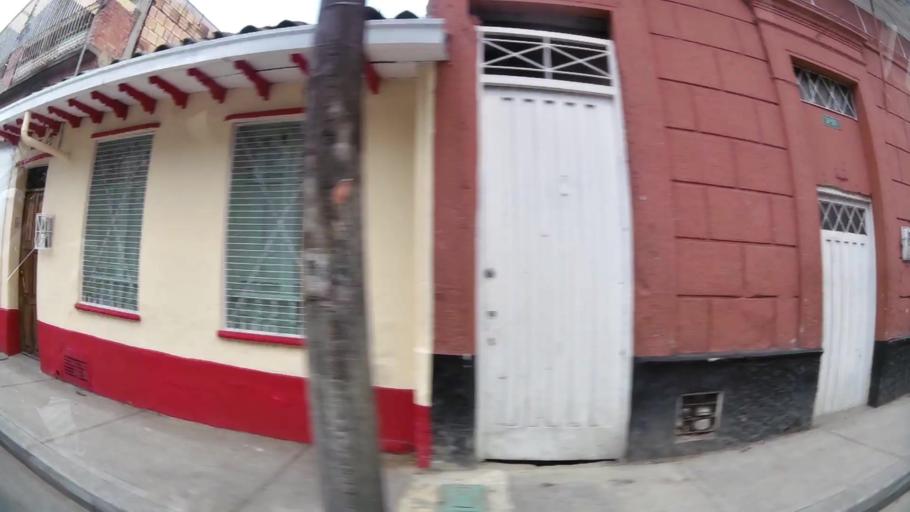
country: CO
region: Bogota D.C.
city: Bogota
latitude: 4.5890
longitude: -74.0794
